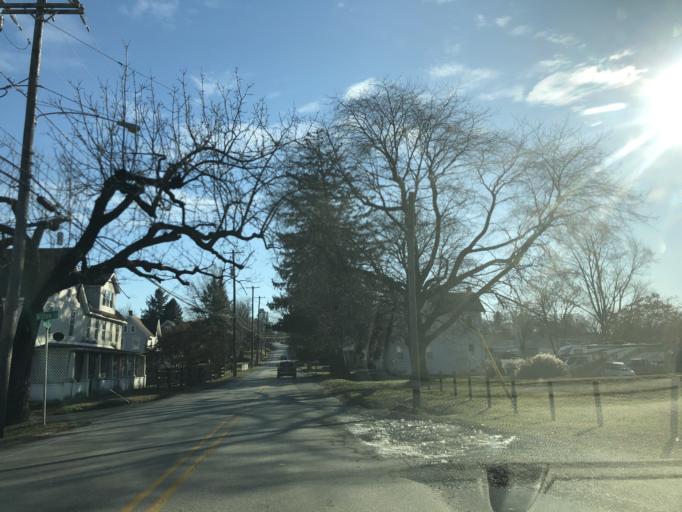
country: US
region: Pennsylvania
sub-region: Chester County
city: Toughkenamon
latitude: 39.8303
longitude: -75.7570
